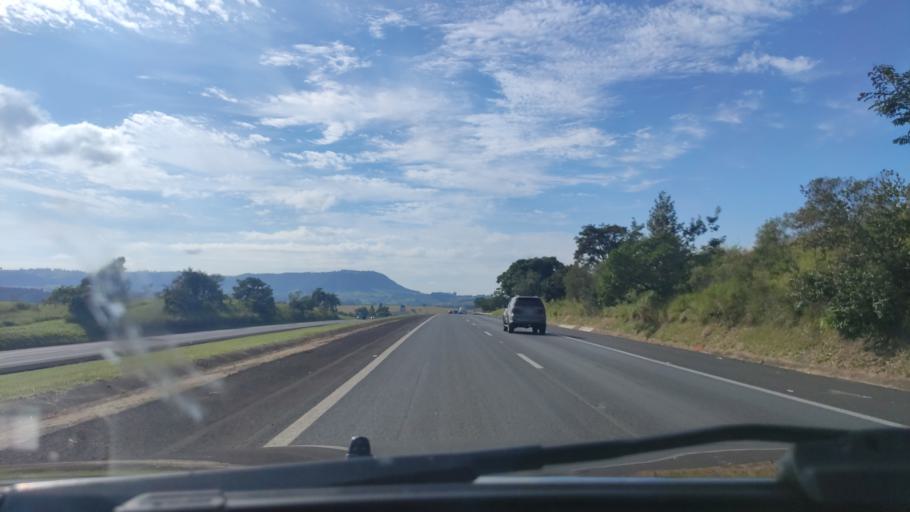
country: BR
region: Sao Paulo
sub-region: Itatinga
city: Itatinga
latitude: -23.1445
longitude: -48.4121
